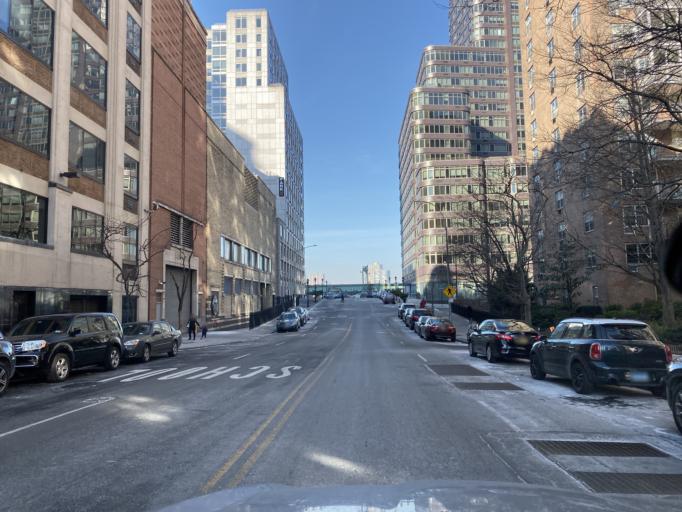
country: US
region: New Jersey
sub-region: Hudson County
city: Guttenberg
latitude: 40.7762
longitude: -73.9877
